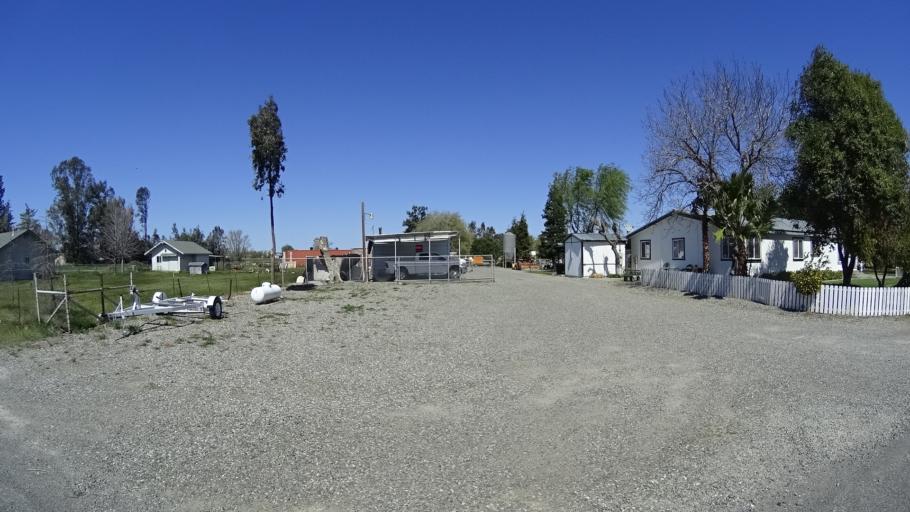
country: US
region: California
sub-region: Glenn County
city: Orland
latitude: 39.7769
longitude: -122.2447
